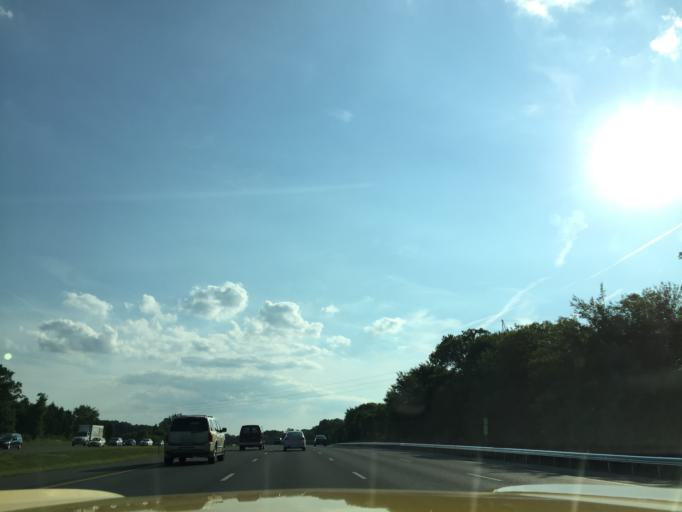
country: US
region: Maryland
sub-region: Baltimore County
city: Kingsville
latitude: 39.4221
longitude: -76.4003
